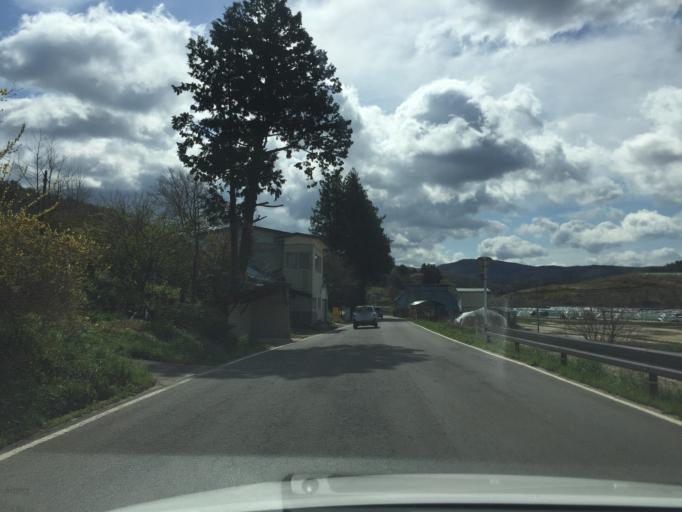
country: JP
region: Fukushima
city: Funehikimachi-funehiki
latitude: 37.6002
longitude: 140.6766
